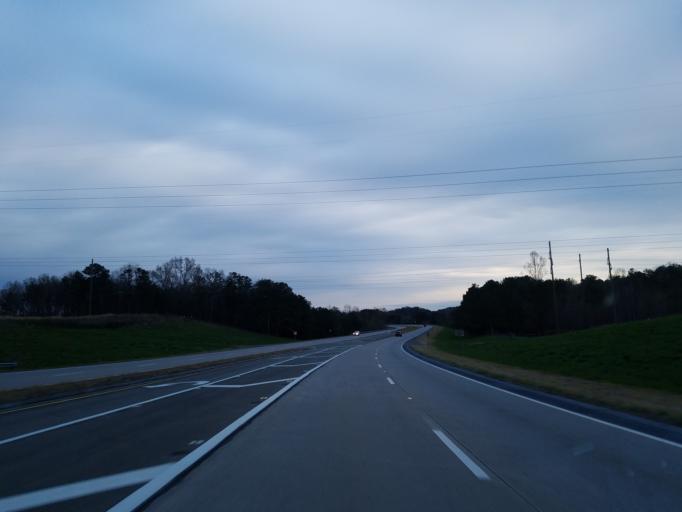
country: US
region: Georgia
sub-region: Gilmer County
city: Ellijay
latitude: 34.5950
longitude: -84.5188
